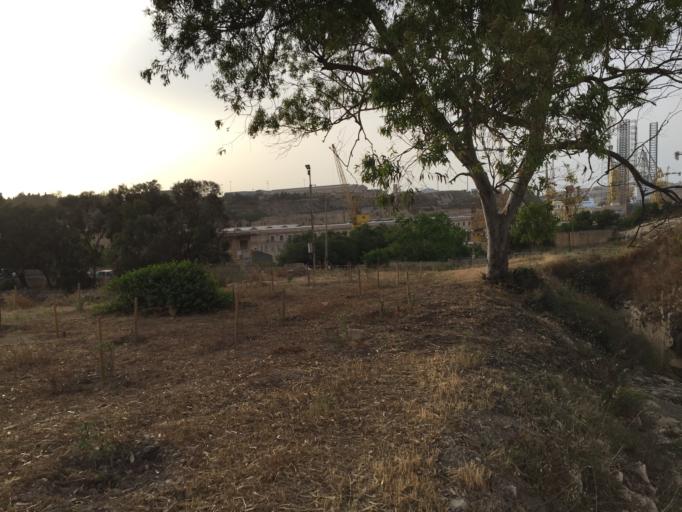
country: MT
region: Il-Fgura
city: Fgura
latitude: 35.8774
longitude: 14.5168
